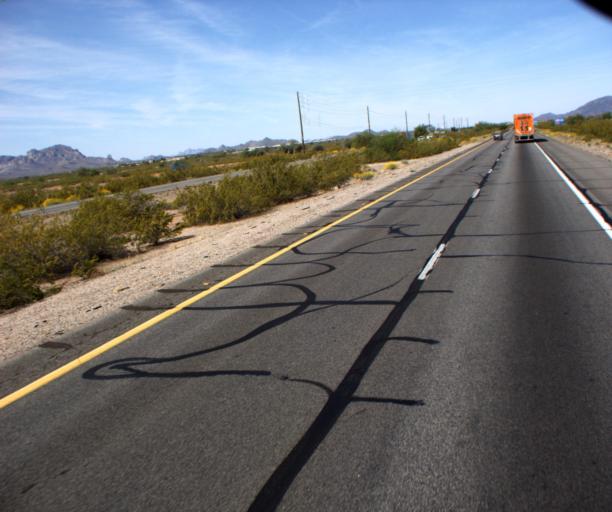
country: US
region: Arizona
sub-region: Maricopa County
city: Buckeye
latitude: 33.4924
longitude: -112.9141
